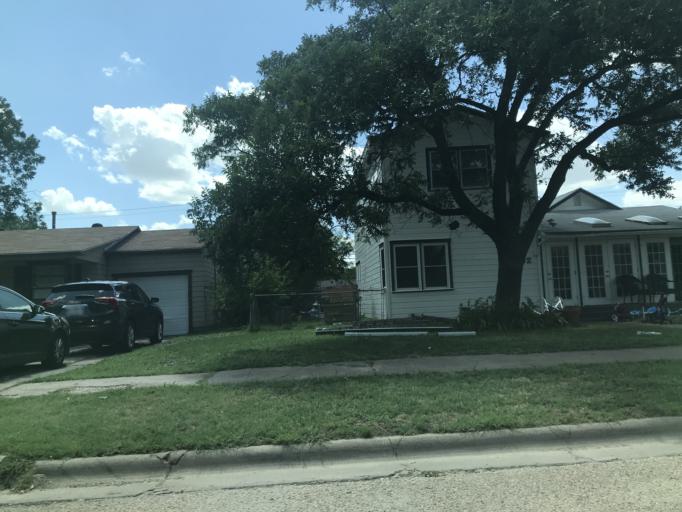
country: US
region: Texas
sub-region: Taylor County
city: Abilene
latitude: 32.4268
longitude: -99.7624
